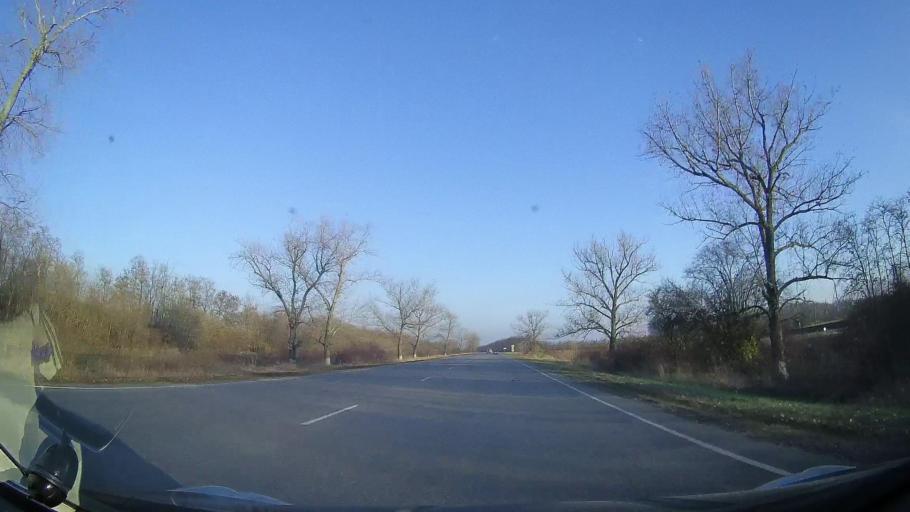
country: RU
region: Rostov
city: Kirovskaya
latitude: 47.0076
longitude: 39.9501
